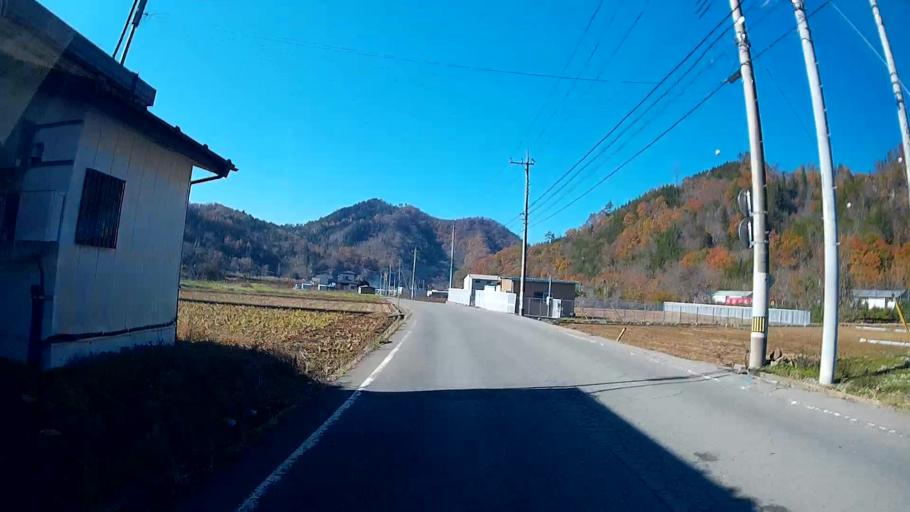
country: JP
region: Yamanashi
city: Otsuki
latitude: 35.5591
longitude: 138.9600
